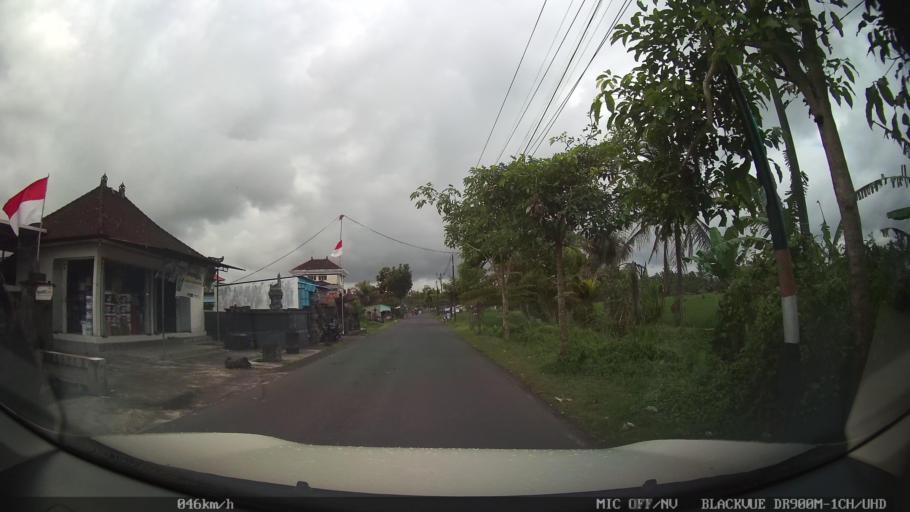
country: ID
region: Bali
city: Banjar Pekenjelodan
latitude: -8.5592
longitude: 115.1890
